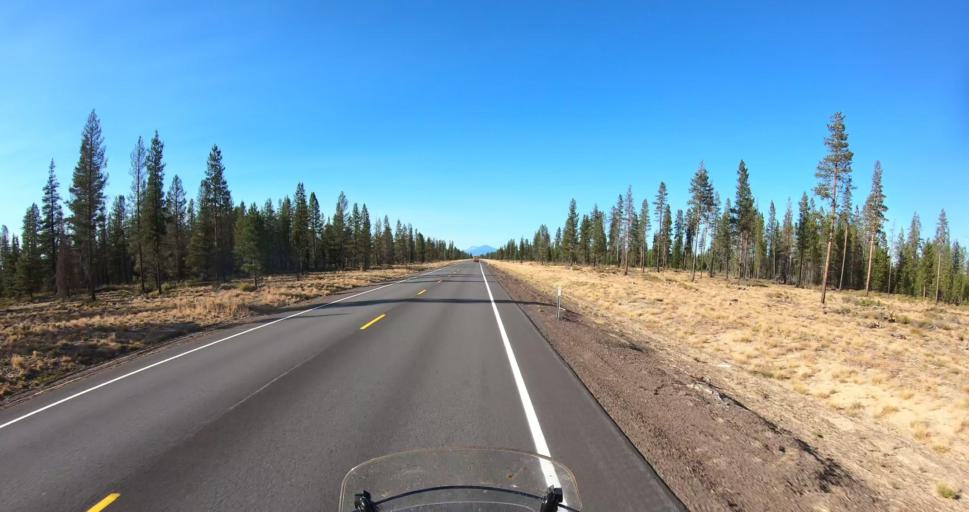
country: US
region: Oregon
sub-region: Deschutes County
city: La Pine
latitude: 43.5785
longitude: -121.4861
